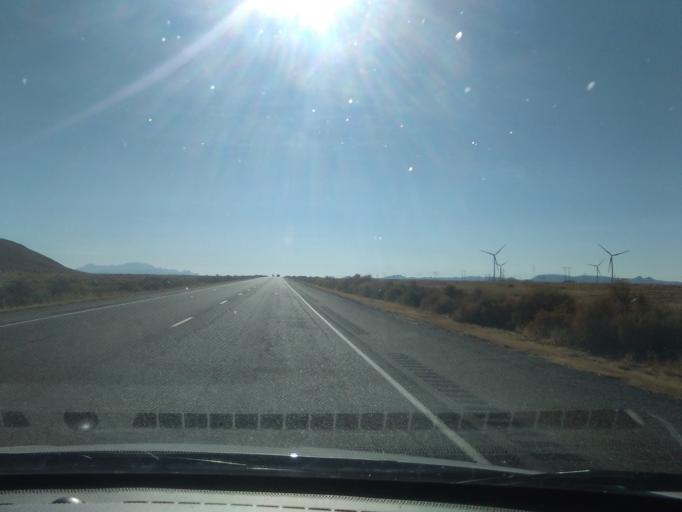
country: US
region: New Mexico
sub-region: Dona Ana County
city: Hatch
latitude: 32.5493
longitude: -107.4778
